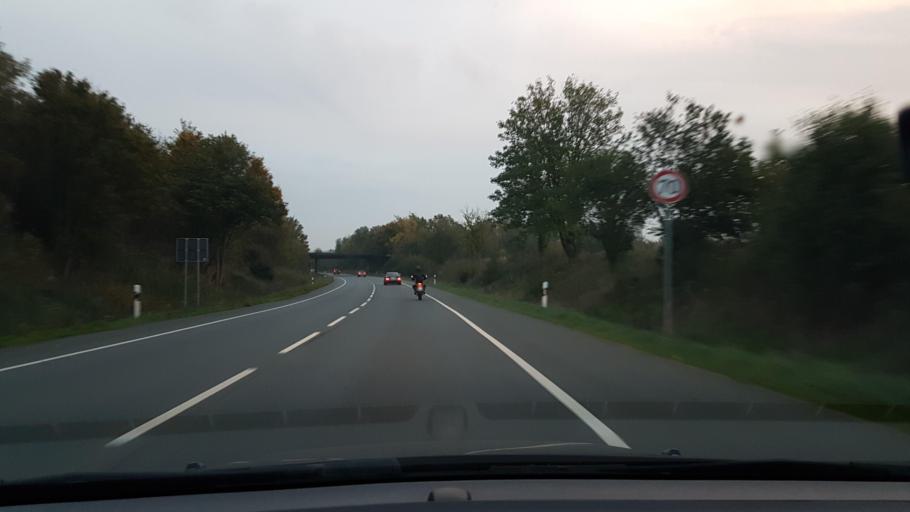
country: DE
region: Lower Saxony
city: Wunstorf
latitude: 52.4254
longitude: 9.4607
